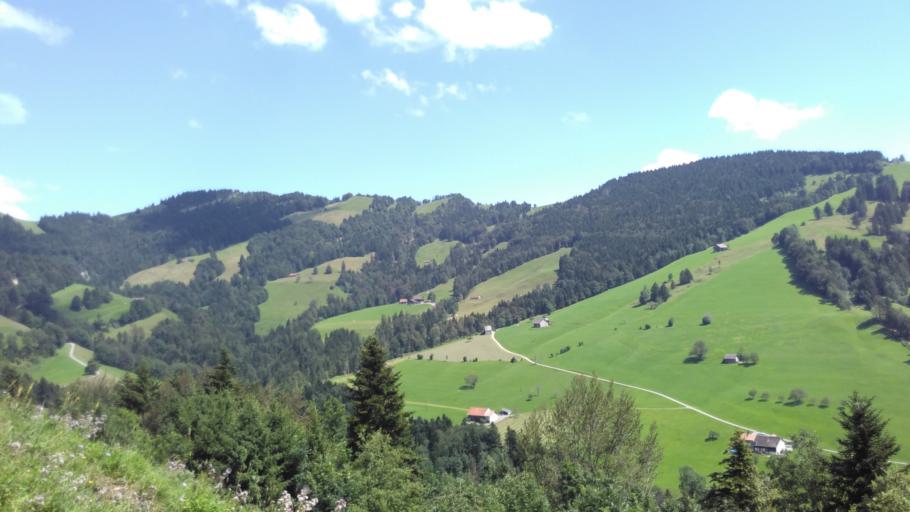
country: CH
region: Saint Gallen
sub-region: Wahlkreis See-Gaster
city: Goldingen
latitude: 47.2910
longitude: 8.9945
